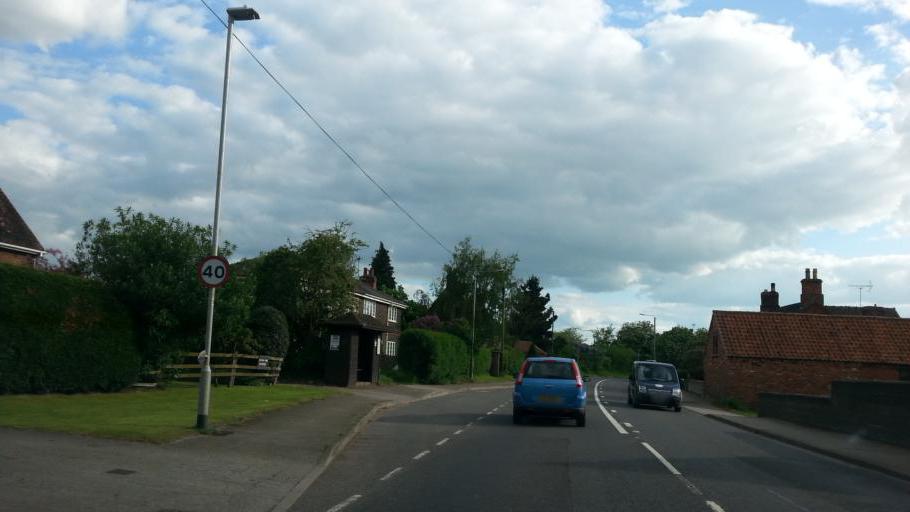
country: GB
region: England
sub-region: Nottinghamshire
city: South Collingham
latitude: 53.1164
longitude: -0.7725
